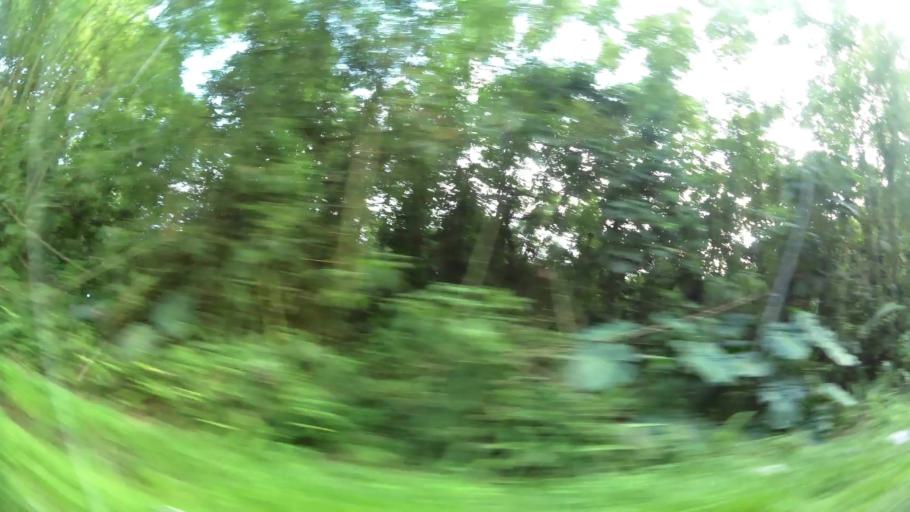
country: GP
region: Guadeloupe
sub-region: Guadeloupe
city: Bouillante
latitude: 16.1790
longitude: -61.7089
